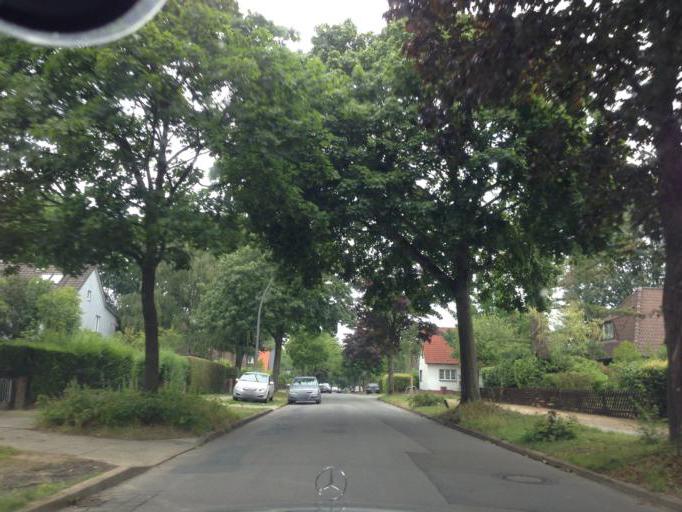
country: DE
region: Hamburg
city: Wandsbek
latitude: 53.5704
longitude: 10.0988
